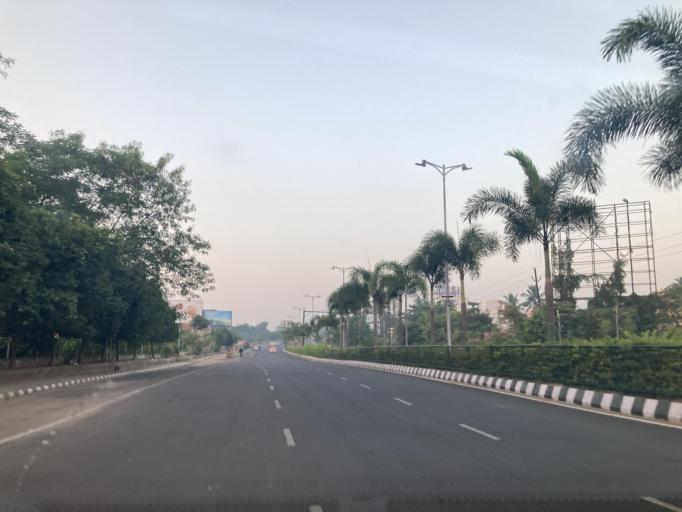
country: IN
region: Odisha
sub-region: Khordha
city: Bhubaneshwar
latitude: 20.2567
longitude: 85.8224
